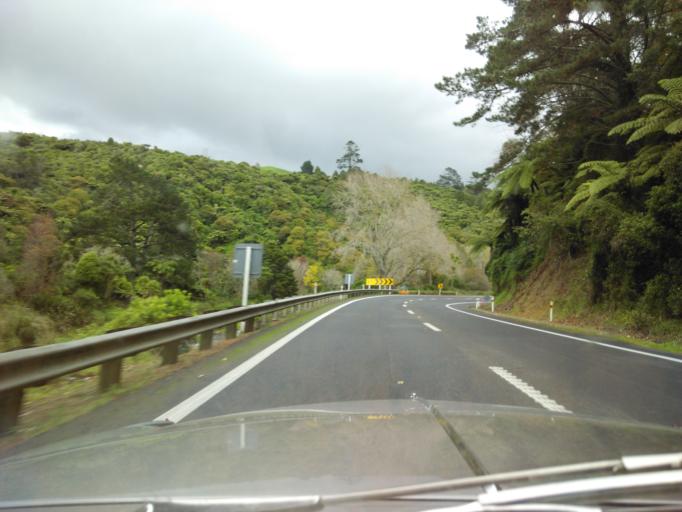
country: NZ
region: Waikato
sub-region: Hauraki District
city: Waihi
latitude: -37.4184
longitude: 175.7533
